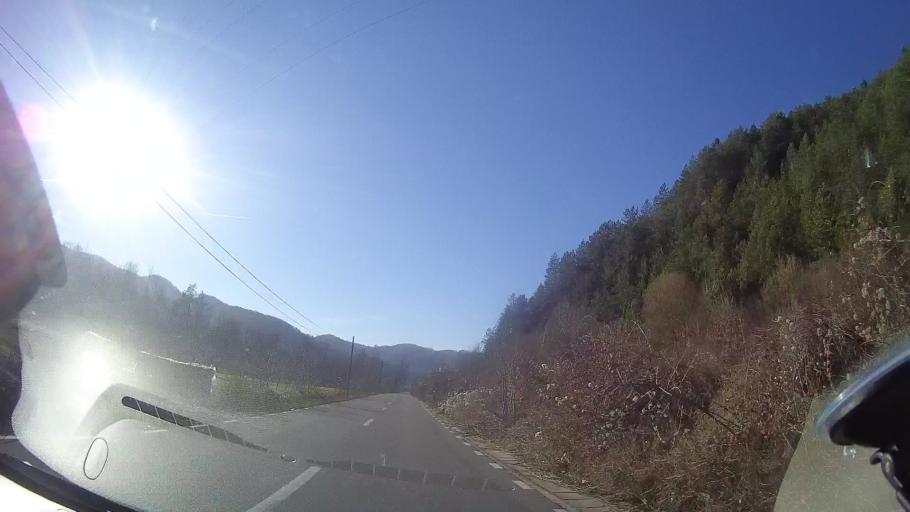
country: RO
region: Bihor
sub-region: Comuna Bratca
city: Bratca
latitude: 46.9268
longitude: 22.6306
